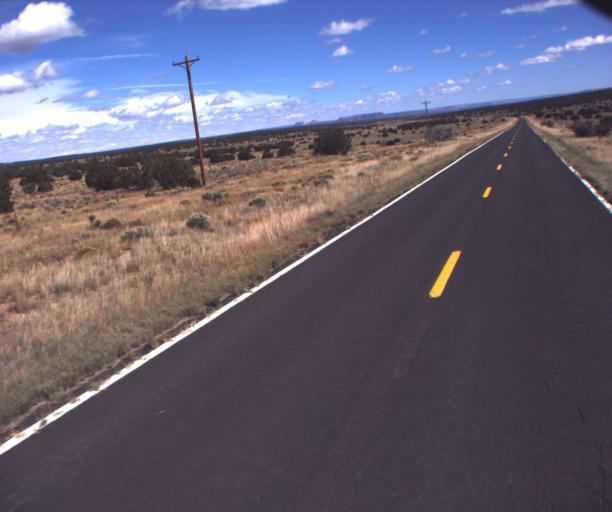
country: US
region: New Mexico
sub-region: McKinley County
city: Zuni Pueblo
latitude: 34.9893
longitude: -109.1120
